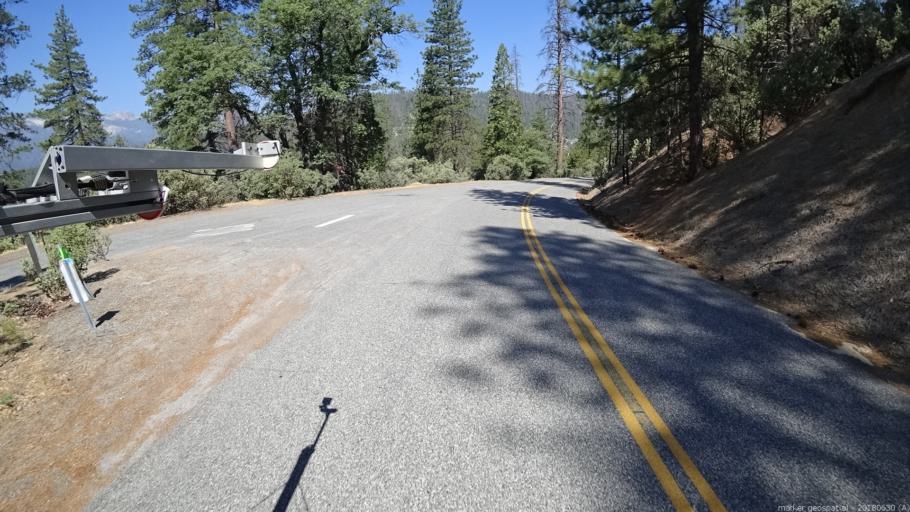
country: US
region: California
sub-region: Madera County
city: Oakhurst
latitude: 37.3822
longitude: -119.3615
